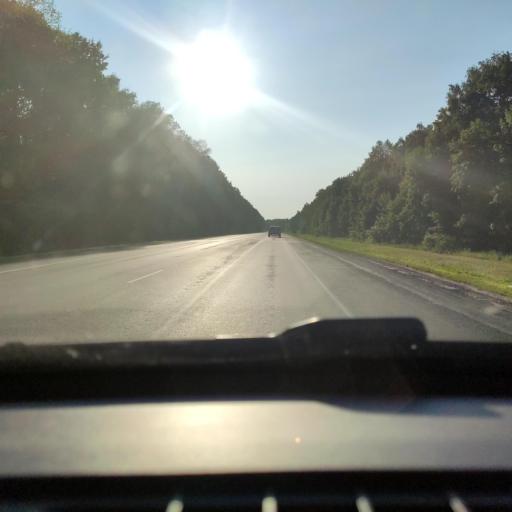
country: RU
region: Voronezj
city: Kashirskoye
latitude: 51.4864
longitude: 39.6481
